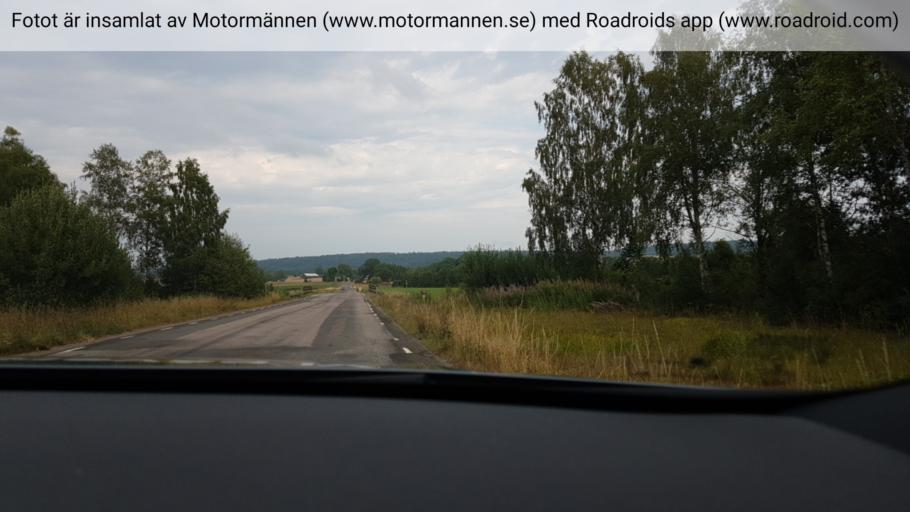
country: SE
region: Vaestra Goetaland
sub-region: Falkopings Kommun
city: Akarp
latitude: 58.1795
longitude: 13.6736
